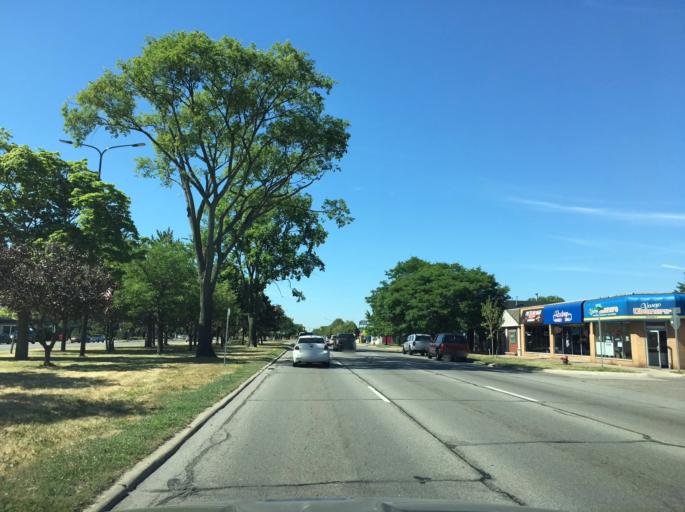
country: US
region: Michigan
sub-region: Macomb County
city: Eastpointe
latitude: 42.4699
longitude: -82.9547
